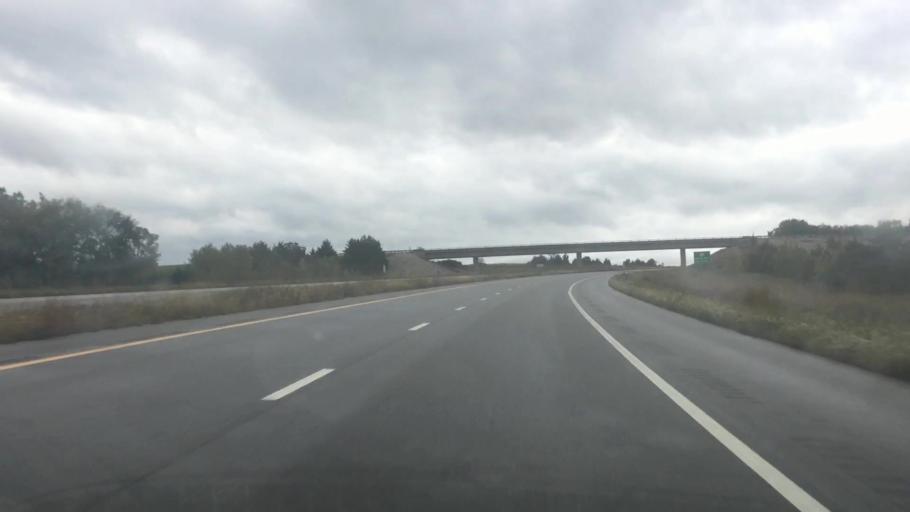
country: US
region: Kansas
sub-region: Miami County
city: Osawatomie
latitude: 38.4713
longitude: -94.9466
